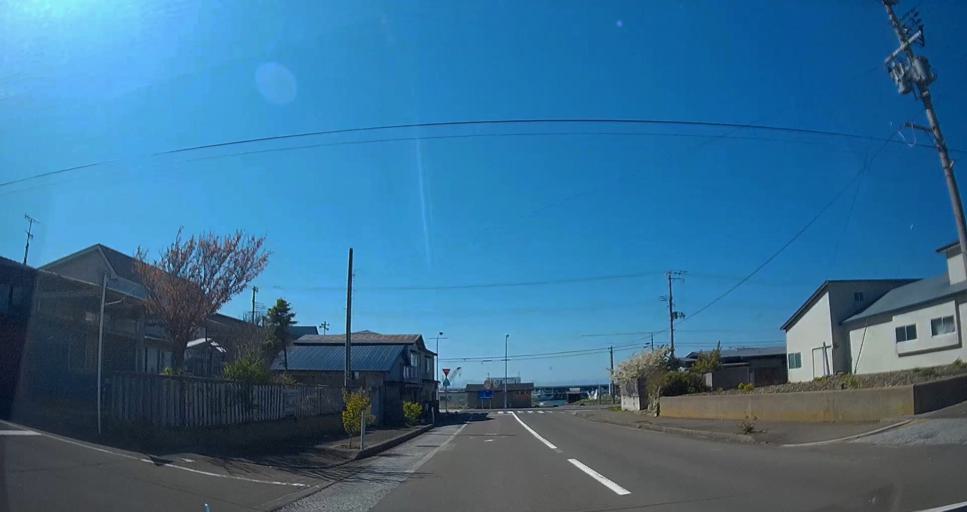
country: JP
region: Hokkaido
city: Hakodate
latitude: 41.5239
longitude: 140.9021
